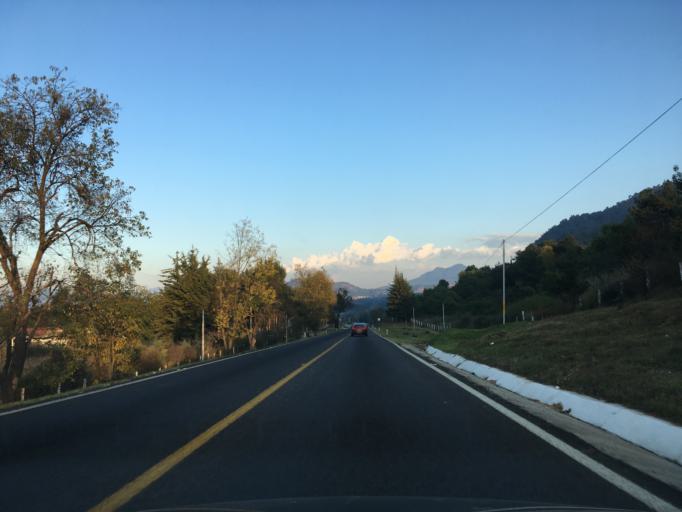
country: MX
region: Michoacan
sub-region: Patzcuaro
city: Santa Ana Chapitiro
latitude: 19.5226
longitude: -101.6597
